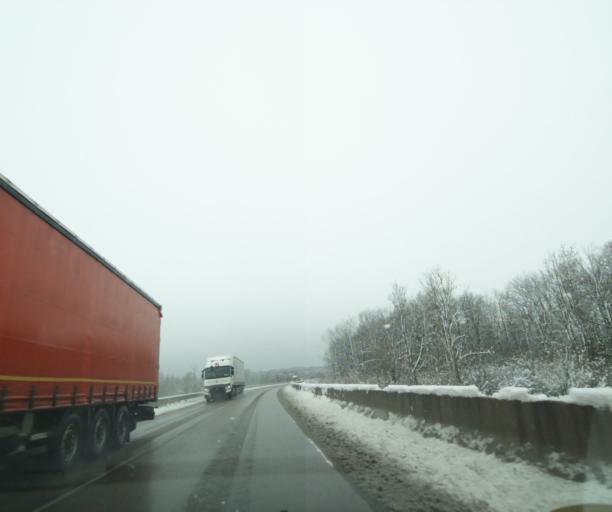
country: FR
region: Champagne-Ardenne
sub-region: Departement de la Haute-Marne
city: Saint-Dizier
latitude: 48.5777
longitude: 4.8818
